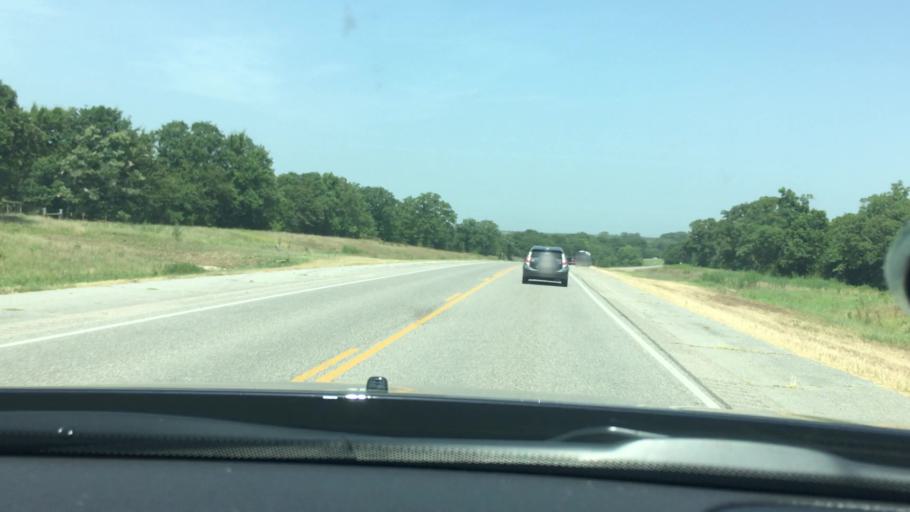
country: US
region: Oklahoma
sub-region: Coal County
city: Coalgate
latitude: 34.6020
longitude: -96.3687
